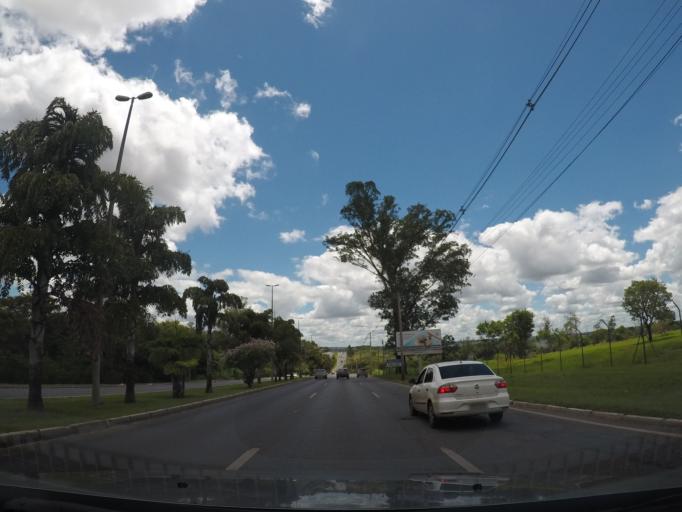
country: BR
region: Federal District
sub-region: Brasilia
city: Brasilia
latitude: -15.8374
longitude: -47.9638
